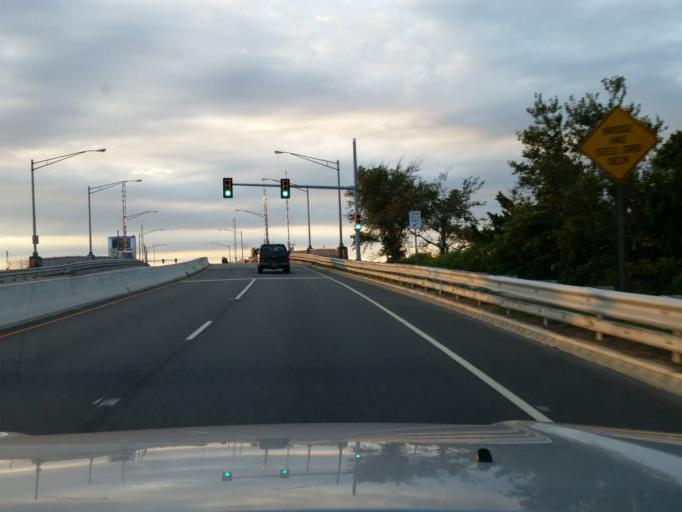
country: US
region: New Jersey
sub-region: Cape May County
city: Wildwood Crest
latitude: 38.9904
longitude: -74.8323
